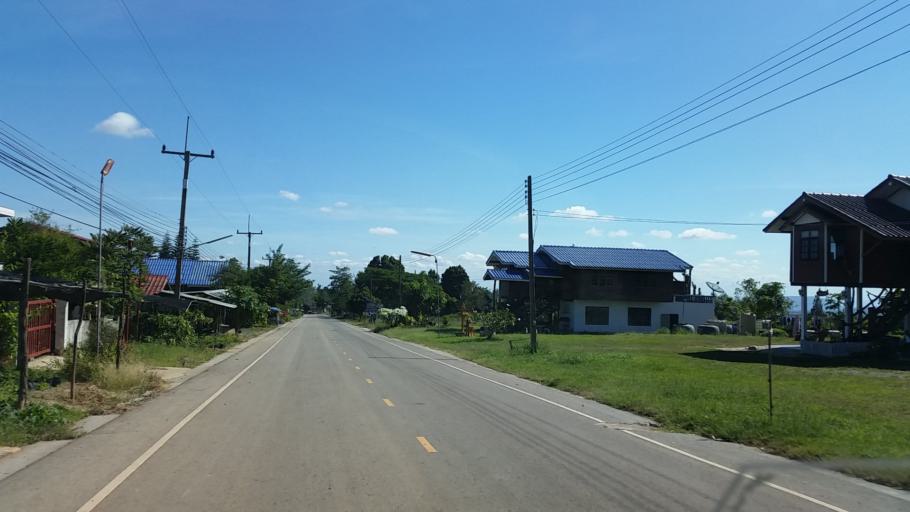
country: TH
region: Chaiyaphum
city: Sap Yai
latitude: 15.6282
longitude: 101.3967
